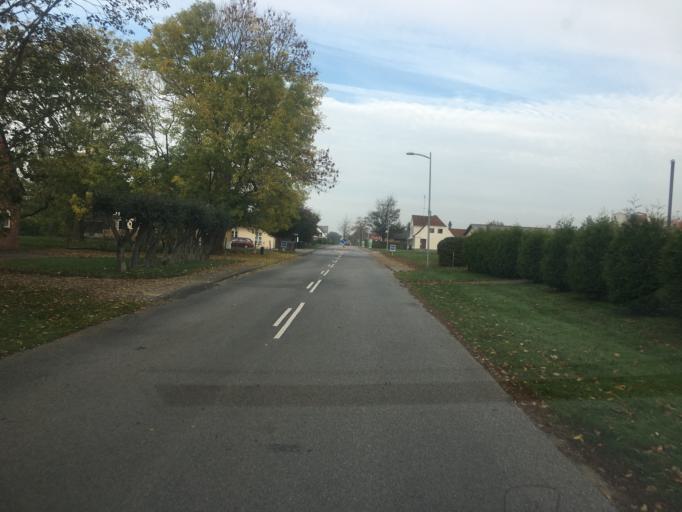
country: DK
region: South Denmark
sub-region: Tonder Kommune
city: Toftlund
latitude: 55.1186
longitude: 9.0718
